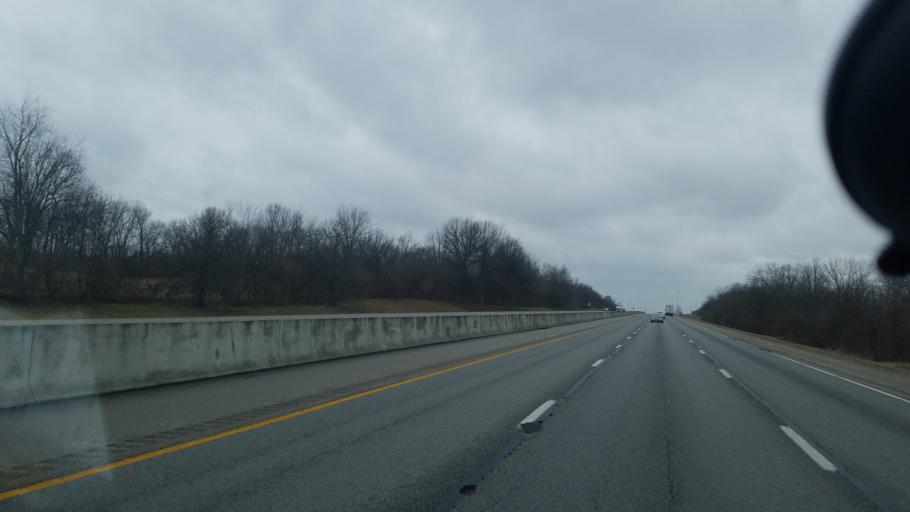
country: US
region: Kentucky
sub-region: Clark County
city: Winchester
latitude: 38.0408
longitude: -84.3060
